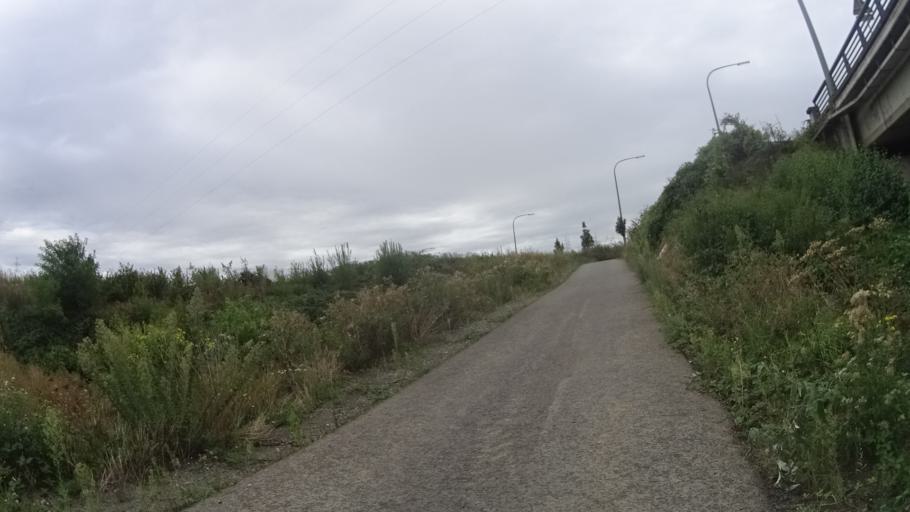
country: BE
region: Wallonia
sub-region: Province de Liege
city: Amay
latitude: 50.5347
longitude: 5.2833
